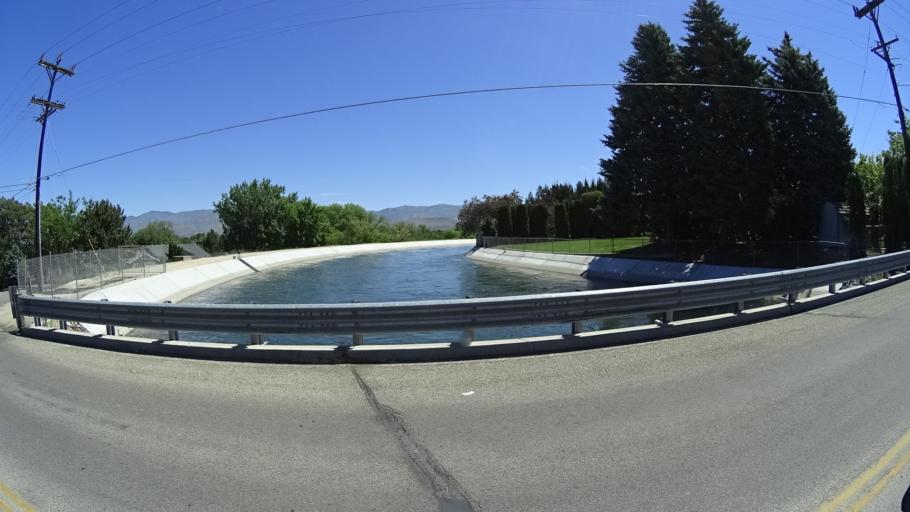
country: US
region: Idaho
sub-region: Ada County
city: Garden City
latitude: 43.5825
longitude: -116.2339
